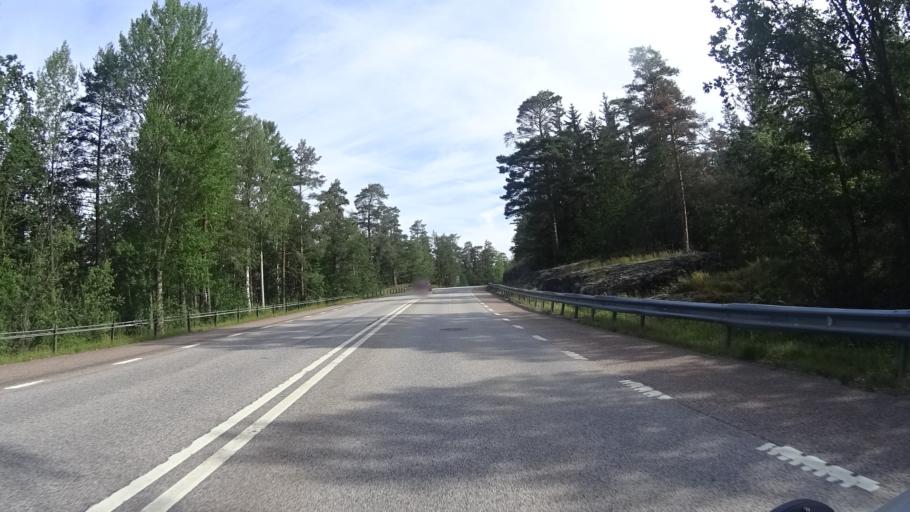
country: SE
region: Kalmar
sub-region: Oskarshamns Kommun
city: Oskarshamn
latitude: 57.4270
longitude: 16.4829
